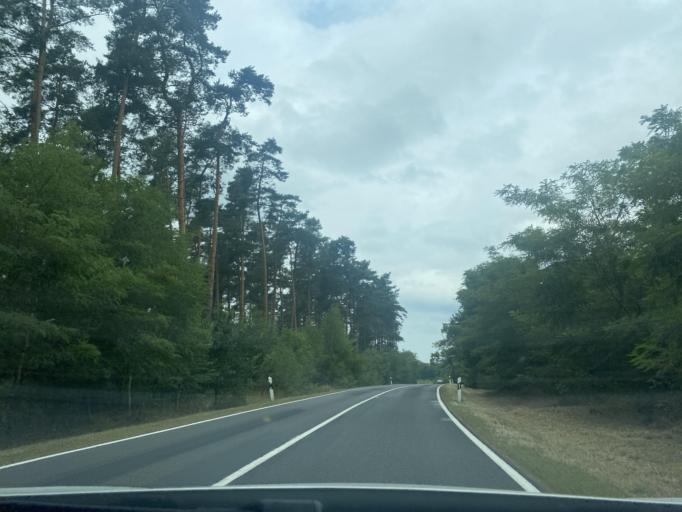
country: DE
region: Saxony
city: Mucka
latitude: 51.2829
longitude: 14.6853
